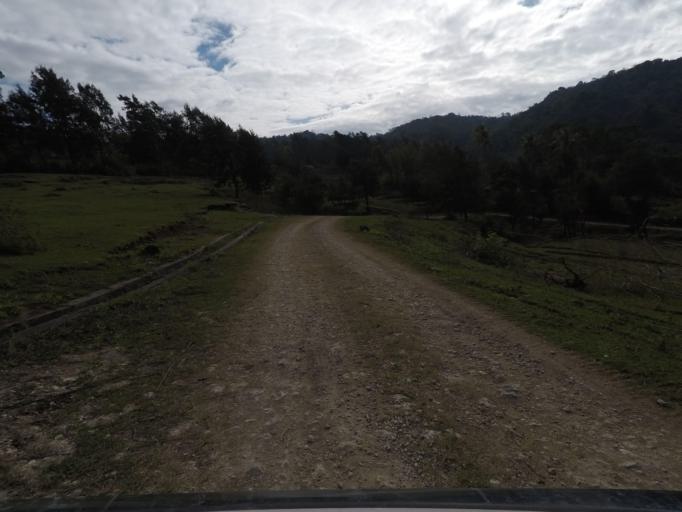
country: TL
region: Baucau
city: Venilale
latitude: -8.6532
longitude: 126.3924
